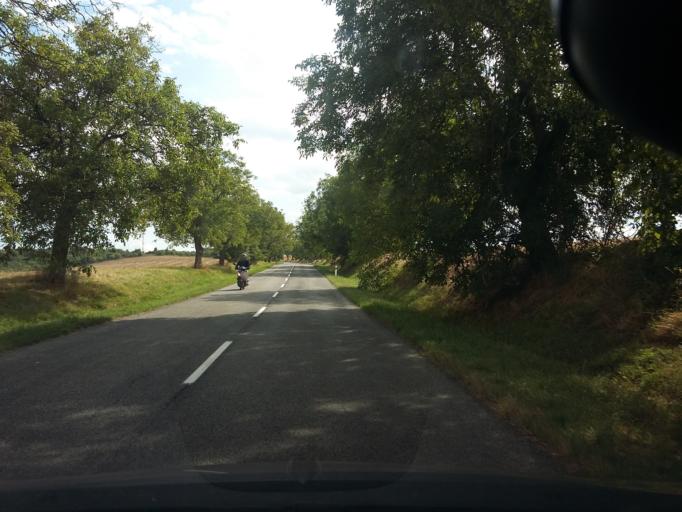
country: SK
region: Trnavsky
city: Gbely
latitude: 48.7139
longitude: 17.1603
